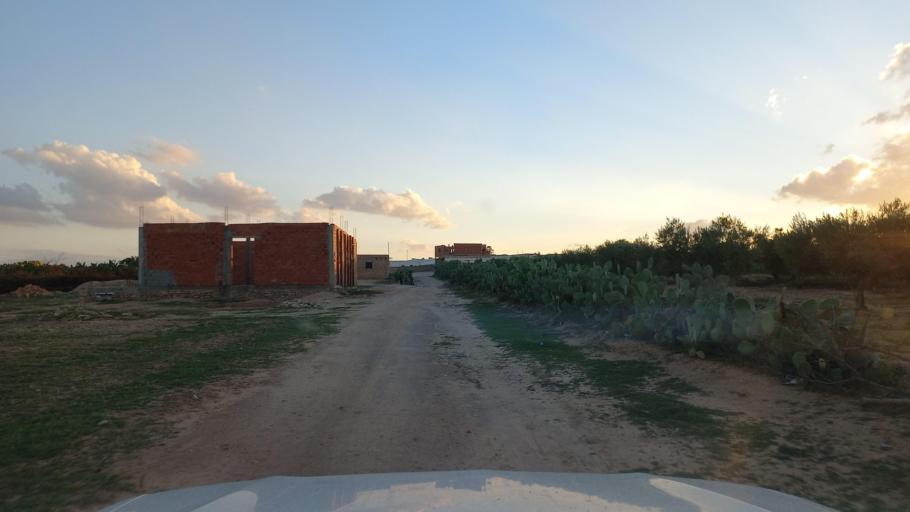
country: TN
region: Al Qasrayn
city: Sbiba
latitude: 35.3688
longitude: 9.0700
